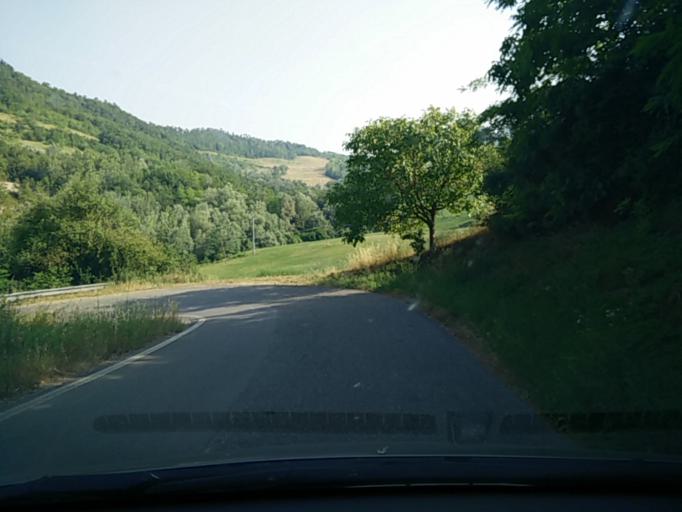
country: IT
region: Lombardy
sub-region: Provincia di Pavia
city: Montesegale
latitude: 44.9307
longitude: 9.1160
